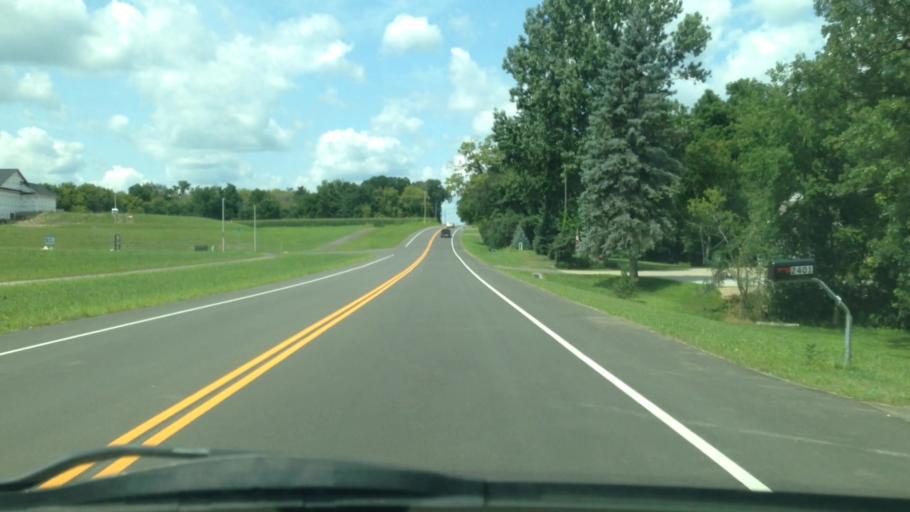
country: US
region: Minnesota
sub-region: Olmsted County
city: Rochester
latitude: 43.9531
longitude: -92.4996
